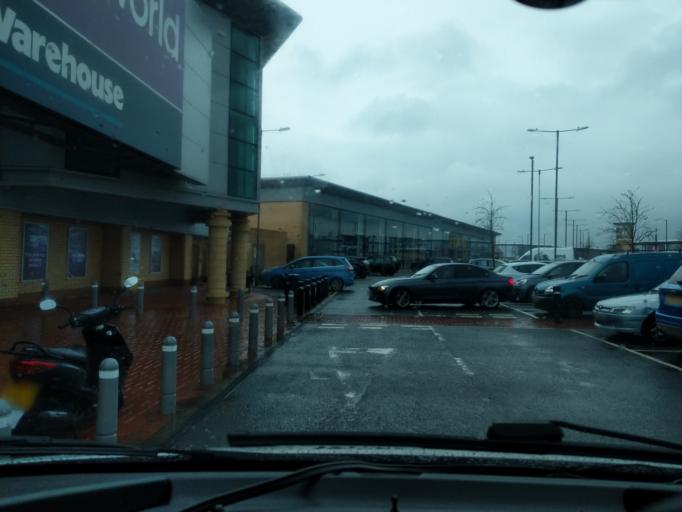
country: GB
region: England
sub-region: St. Helens
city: St Helens
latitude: 53.4466
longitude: -2.7339
